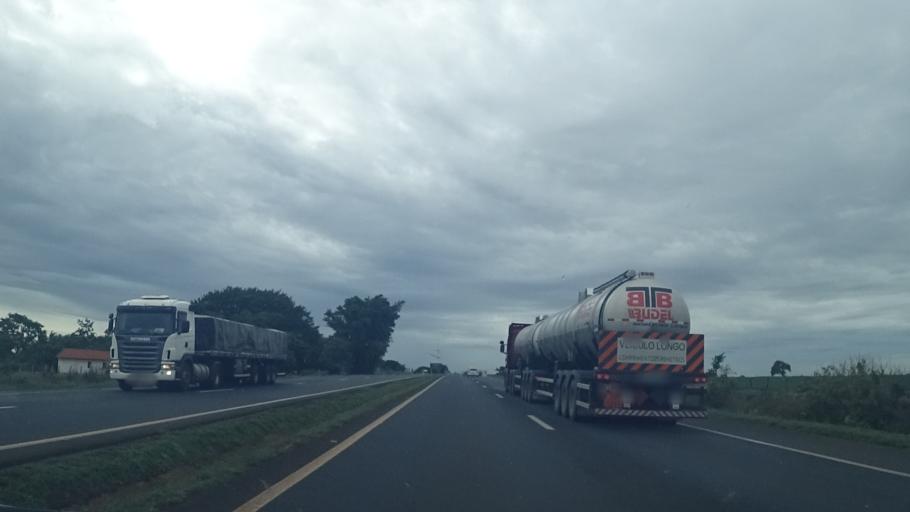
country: BR
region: Minas Gerais
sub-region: Centralina
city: Centralina
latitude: -18.6747
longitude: -49.1590
